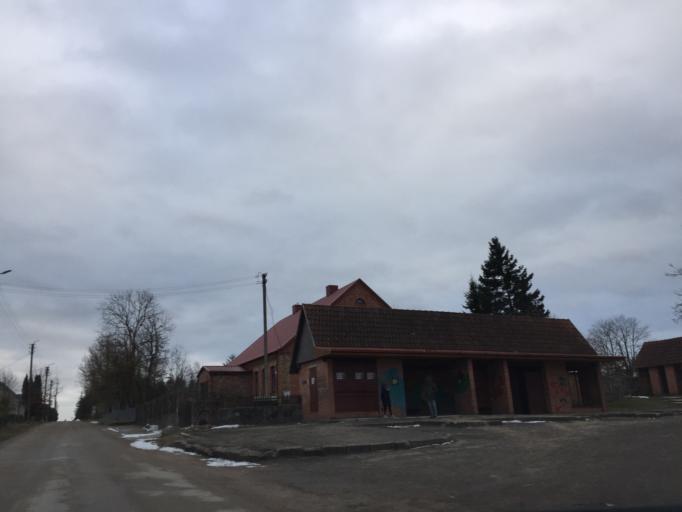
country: LT
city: Zagare
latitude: 56.3569
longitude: 23.2547
